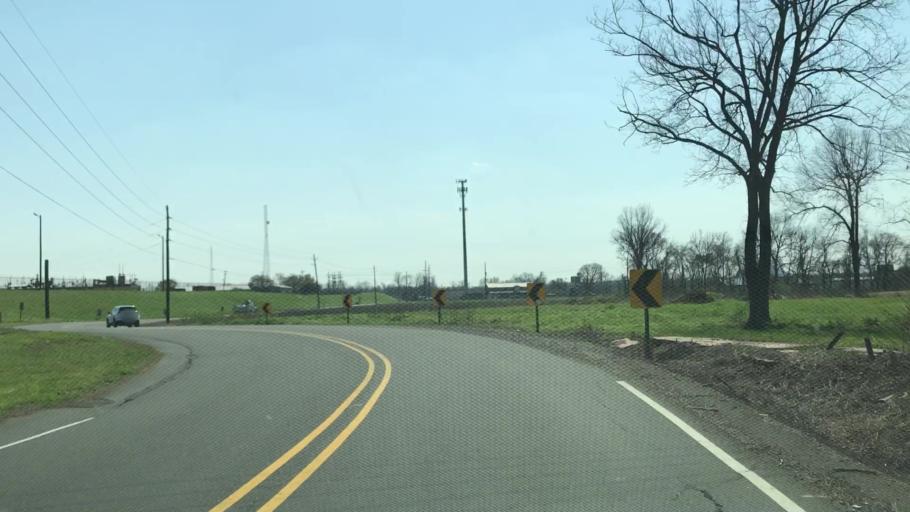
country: US
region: Louisiana
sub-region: Bossier Parish
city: Bossier City
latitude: 32.4045
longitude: -93.6912
